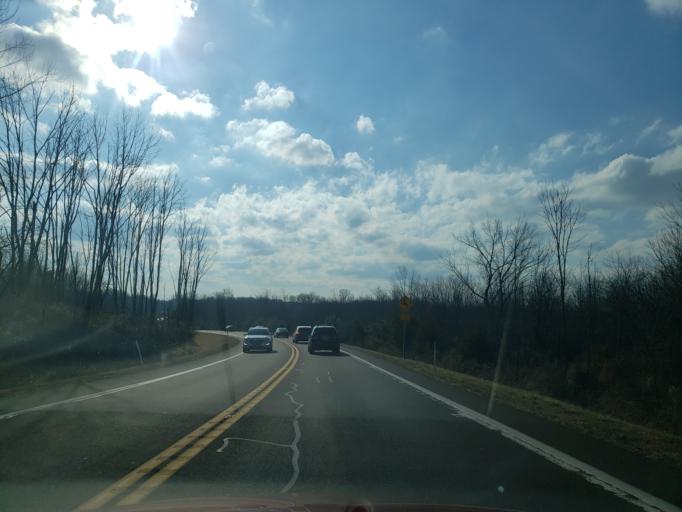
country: US
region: Pennsylvania
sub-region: Bucks County
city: Brittany Farms-Highlands
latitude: 40.2529
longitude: -75.2117
